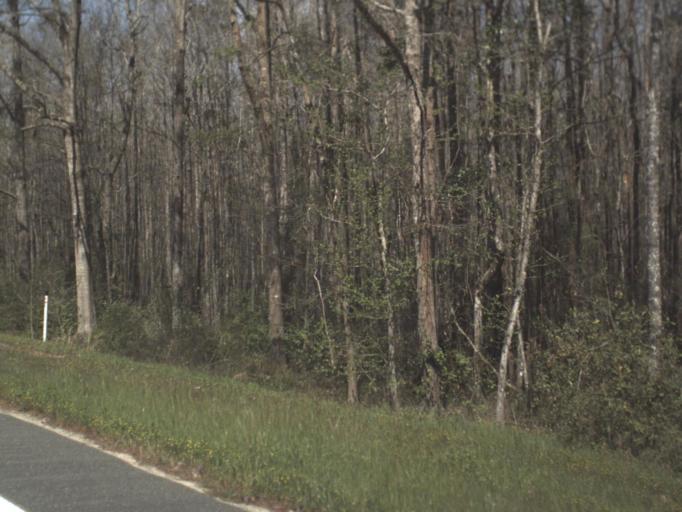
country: US
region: Florida
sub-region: Holmes County
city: Bonifay
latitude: 30.7792
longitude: -85.6266
